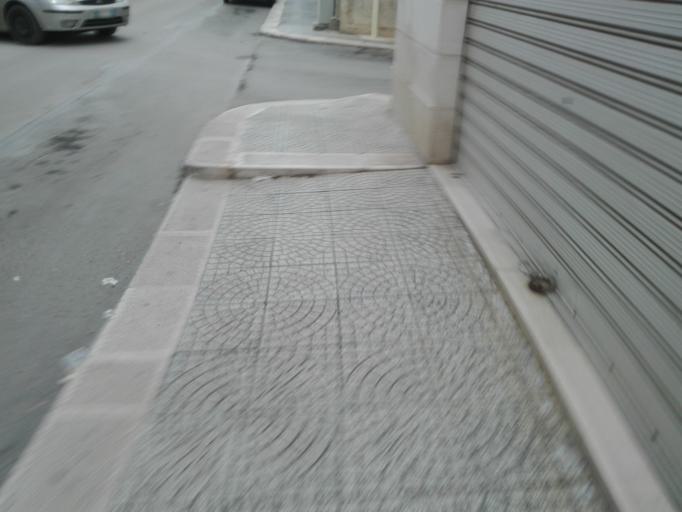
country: IT
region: Apulia
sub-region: Provincia di Bari
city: Corato
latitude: 41.1555
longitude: 16.4097
